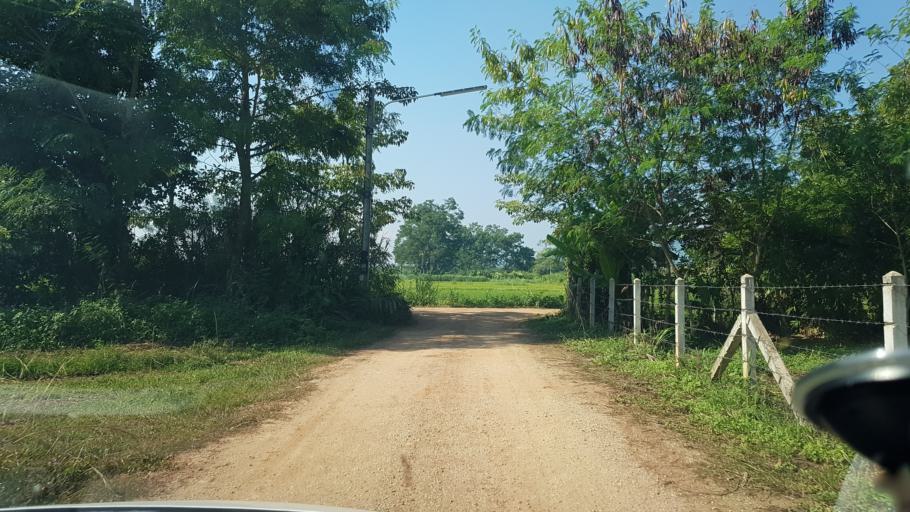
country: TH
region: Chiang Rai
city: Chiang Rai
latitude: 19.9009
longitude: 99.7960
